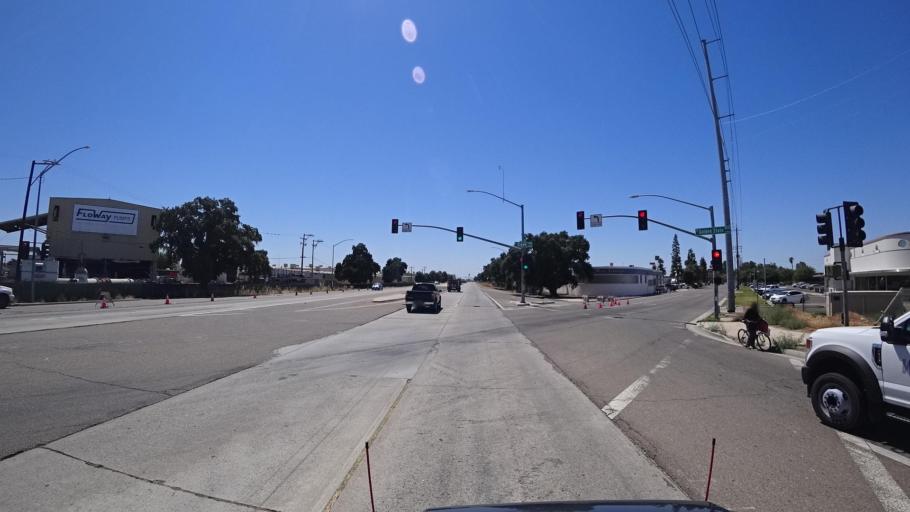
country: US
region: California
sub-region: Fresno County
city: Fresno
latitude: 36.7108
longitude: -119.7728
